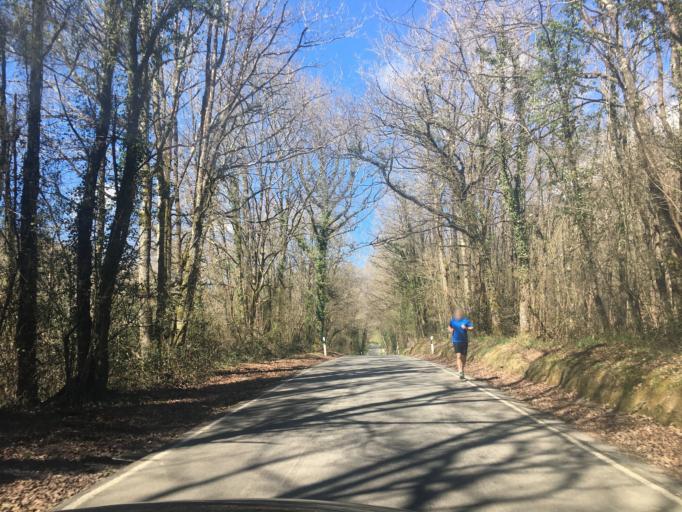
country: ES
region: Basque Country
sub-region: Bizkaia
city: Amorebieta
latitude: 43.2356
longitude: -2.7408
